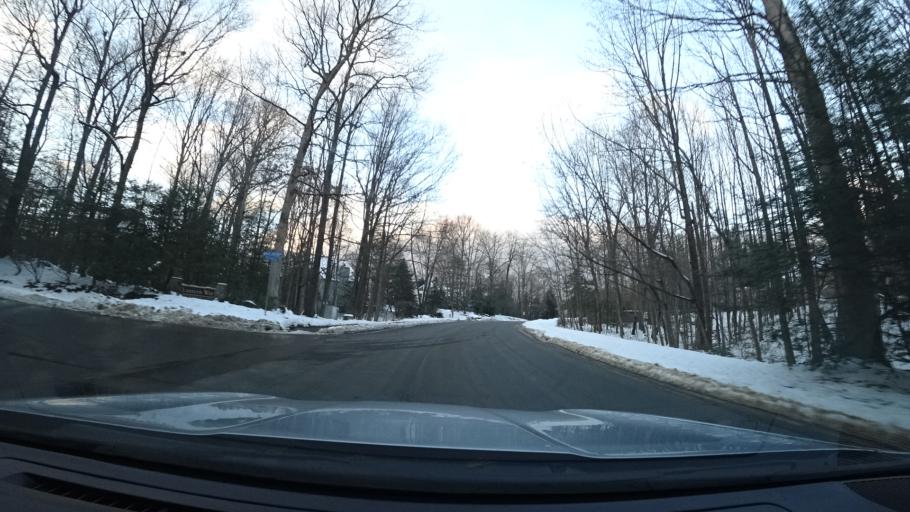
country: US
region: Virginia
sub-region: Fairfax County
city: Reston
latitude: 38.9781
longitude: -77.3448
